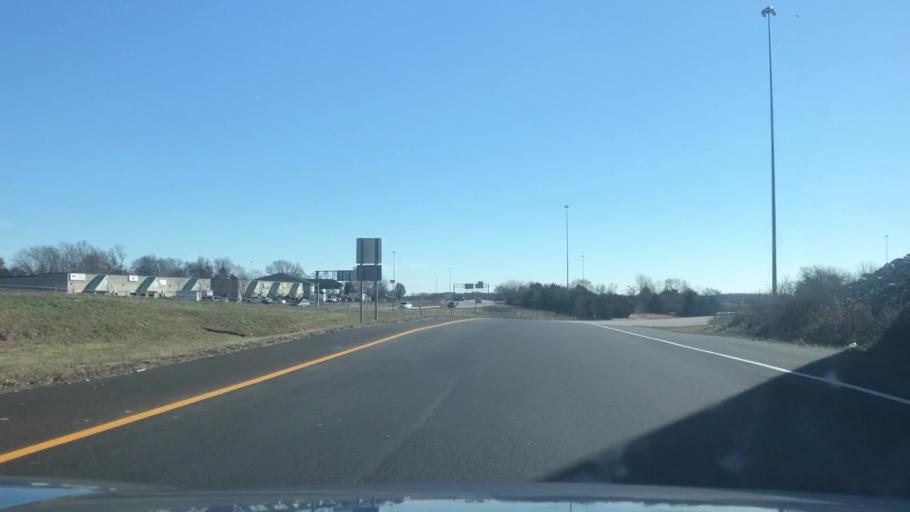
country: US
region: Missouri
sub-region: Saint Charles County
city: Wentzville
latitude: 38.8111
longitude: -90.8416
